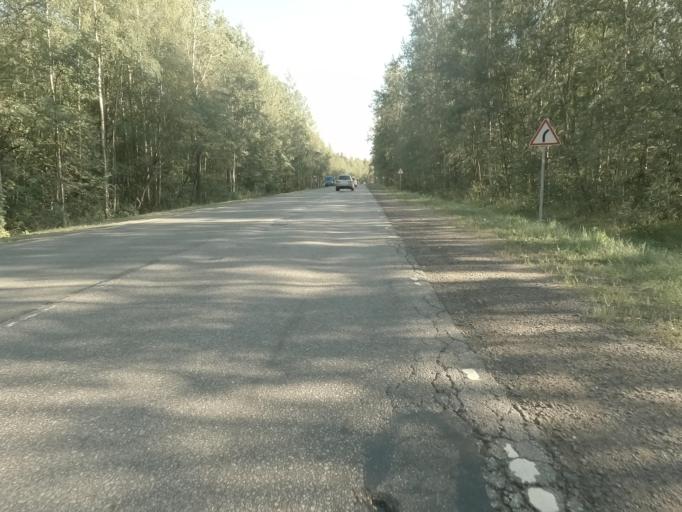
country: RU
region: Leningrad
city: Kirovsk
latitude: 59.9344
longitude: 30.9828
